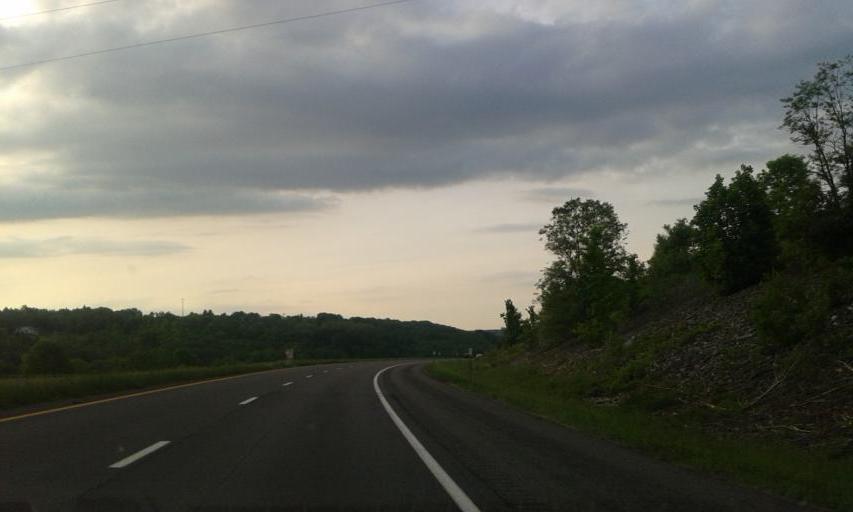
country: US
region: New York
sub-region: Broome County
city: Chenango Bridge
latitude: 42.2275
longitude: -75.9128
